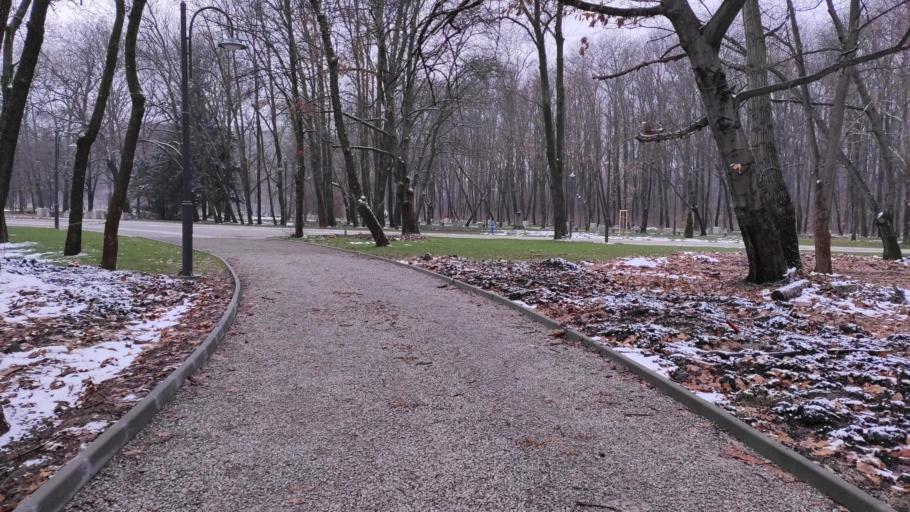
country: BG
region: Sofia-Capital
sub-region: Stolichna Obshtina
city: Sofia
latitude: 42.7128
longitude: 23.2809
